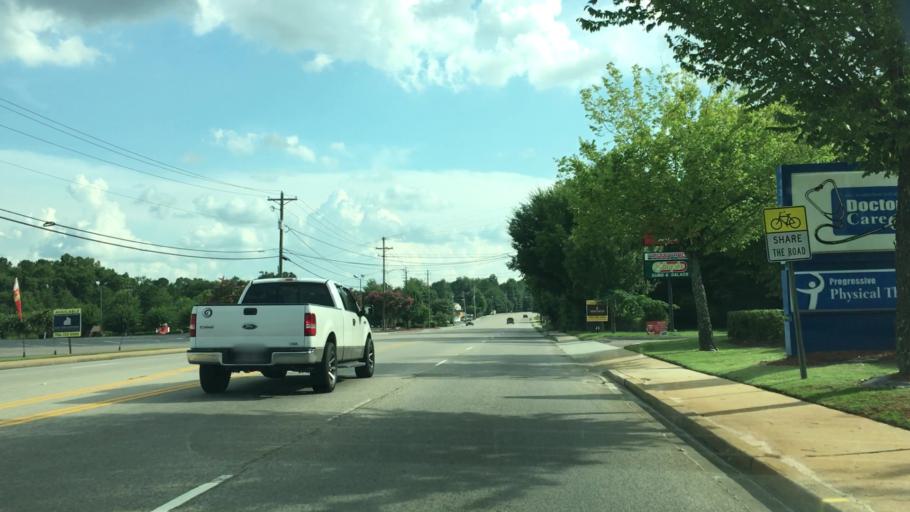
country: US
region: South Carolina
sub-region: Aiken County
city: Aiken
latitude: 33.5760
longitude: -81.7039
